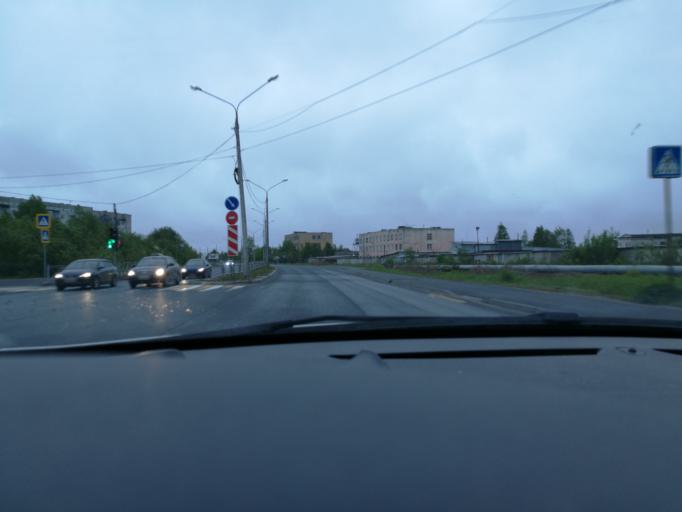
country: RU
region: Arkhangelskaya
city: Severodvinsk
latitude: 64.5667
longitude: 39.7877
